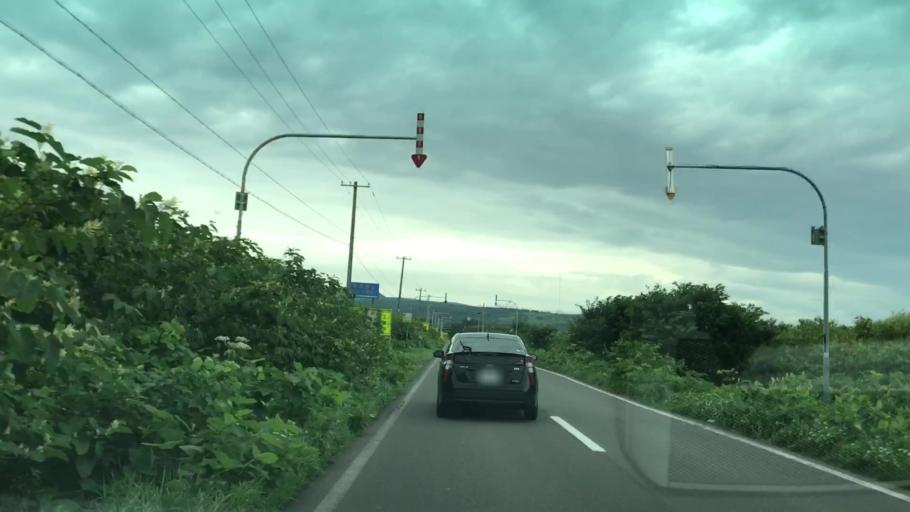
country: JP
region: Hokkaido
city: Iwanai
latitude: 42.8943
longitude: 140.3770
